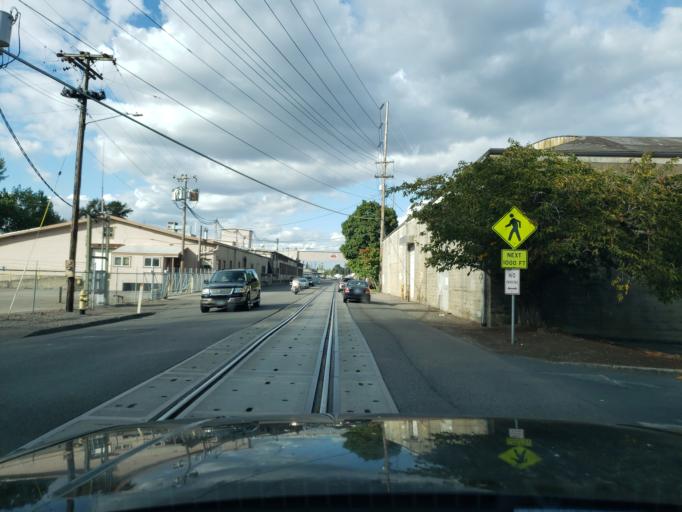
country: US
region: Oregon
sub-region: Marion County
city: Salem
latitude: 44.9510
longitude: -123.0370
